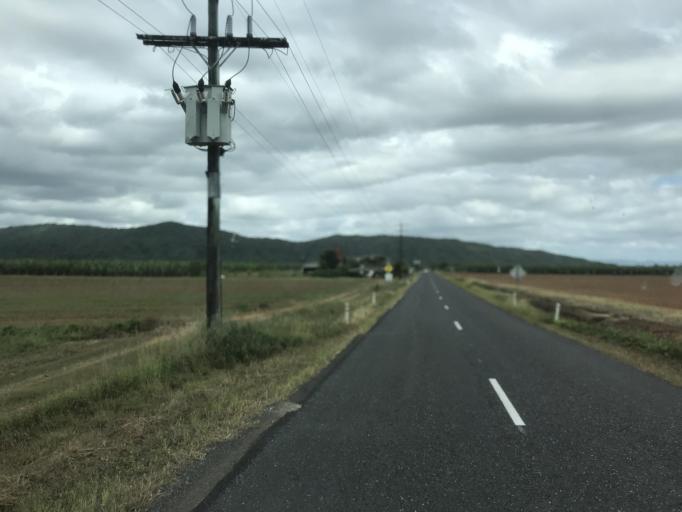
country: AU
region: Queensland
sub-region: Cassowary Coast
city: Innisfail
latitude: -17.6213
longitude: 146.0276
